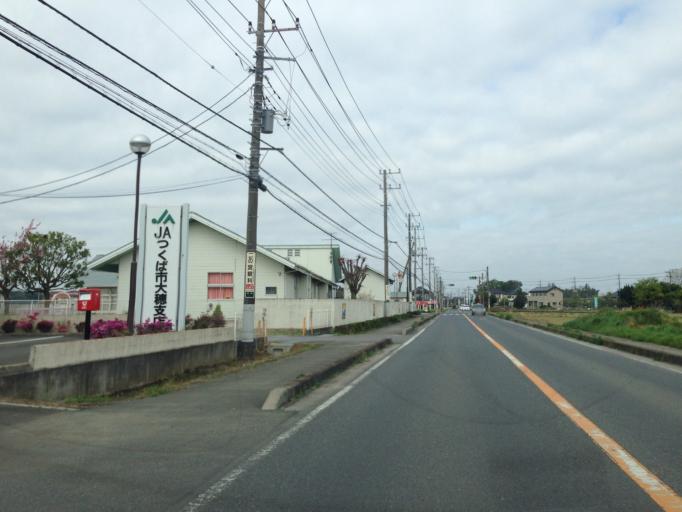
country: JP
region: Ibaraki
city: Tsukuba
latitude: 36.1367
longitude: 140.0613
